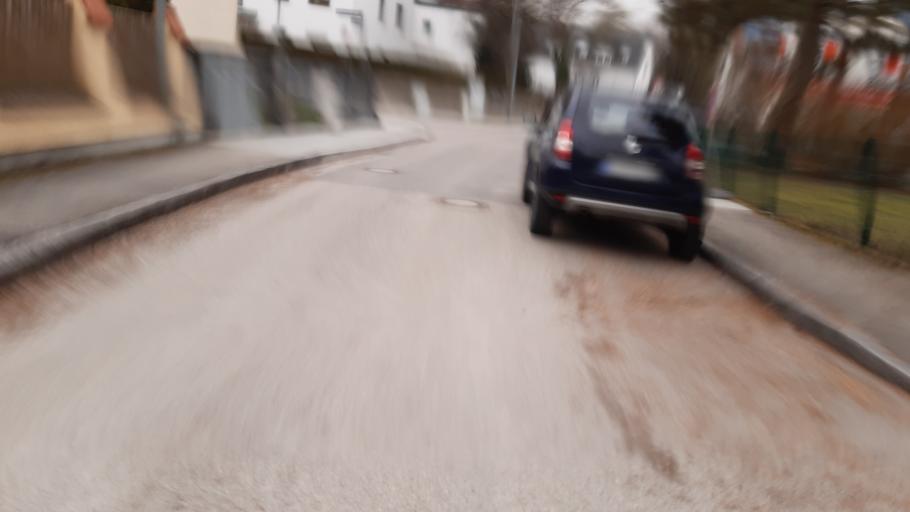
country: DE
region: Bavaria
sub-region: Upper Bavaria
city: Oberschleissheim
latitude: 48.1937
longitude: 11.5302
